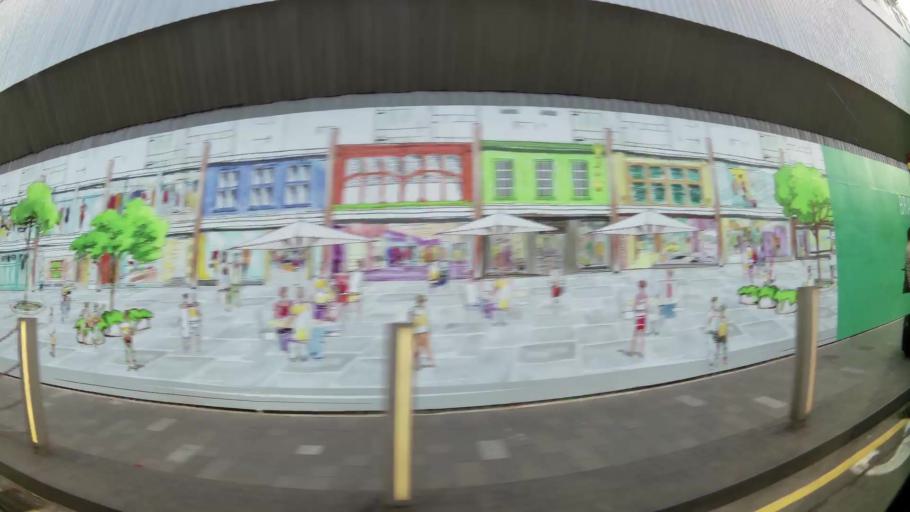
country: HK
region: Wanchai
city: Wan Chai
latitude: 22.2825
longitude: 114.1862
